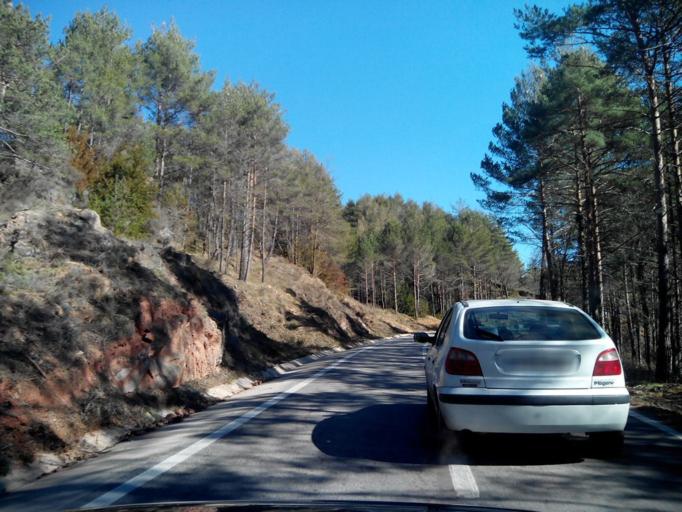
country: ES
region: Catalonia
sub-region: Provincia de Barcelona
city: Borreda
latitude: 42.1380
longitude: 2.0025
